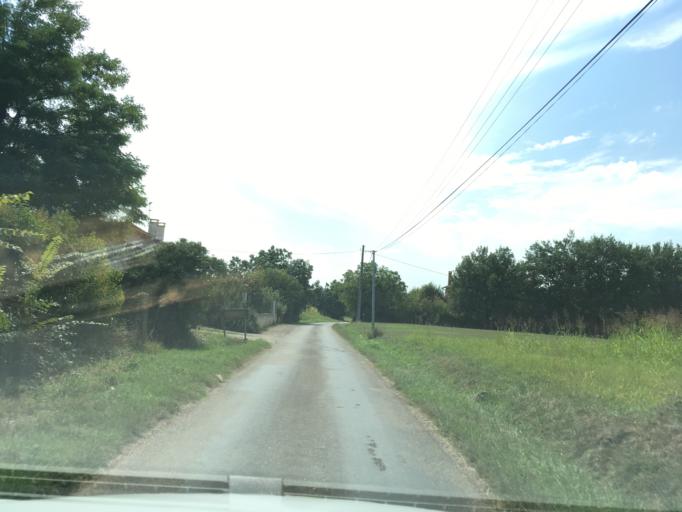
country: FR
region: Midi-Pyrenees
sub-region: Departement du Tarn-et-Garonne
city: Montbeton
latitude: 44.0253
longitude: 1.3141
